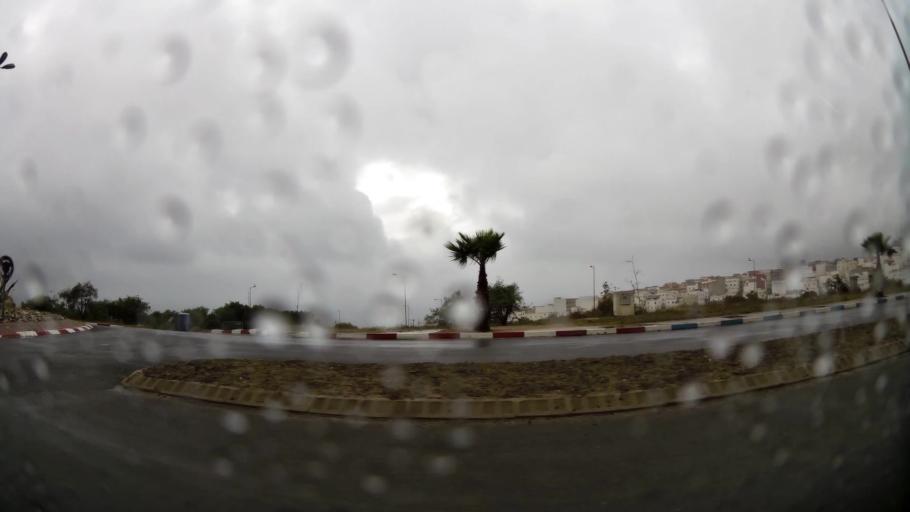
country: MA
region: Taza-Al Hoceima-Taounate
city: Tirhanimine
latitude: 35.2462
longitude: -3.9510
